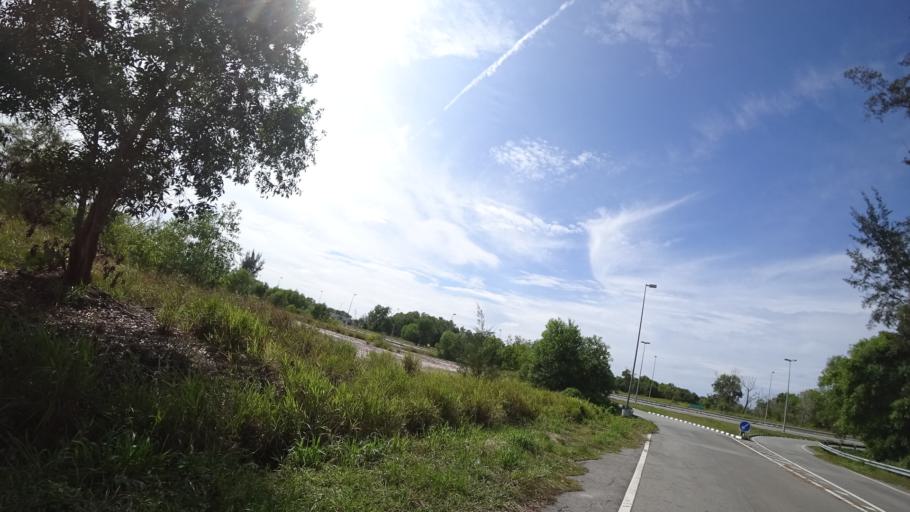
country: BN
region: Tutong
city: Tutong
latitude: 4.8225
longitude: 114.6618
